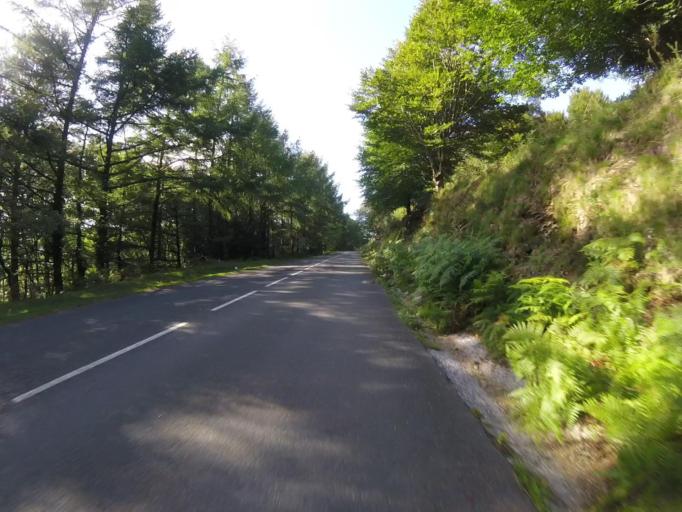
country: ES
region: Basque Country
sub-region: Provincia de Guipuzcoa
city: Irun
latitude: 43.2936
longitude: -1.7776
